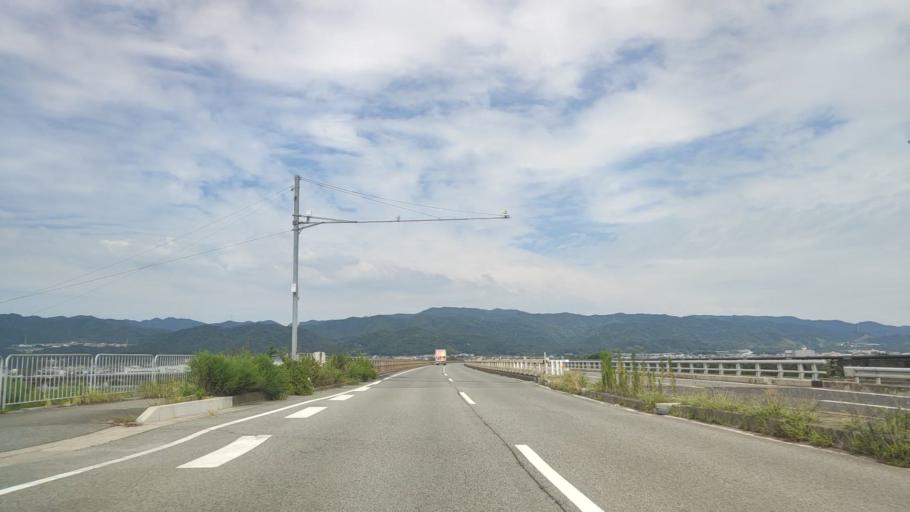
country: JP
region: Wakayama
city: Wakayama-shi
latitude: 34.2485
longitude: 135.2185
